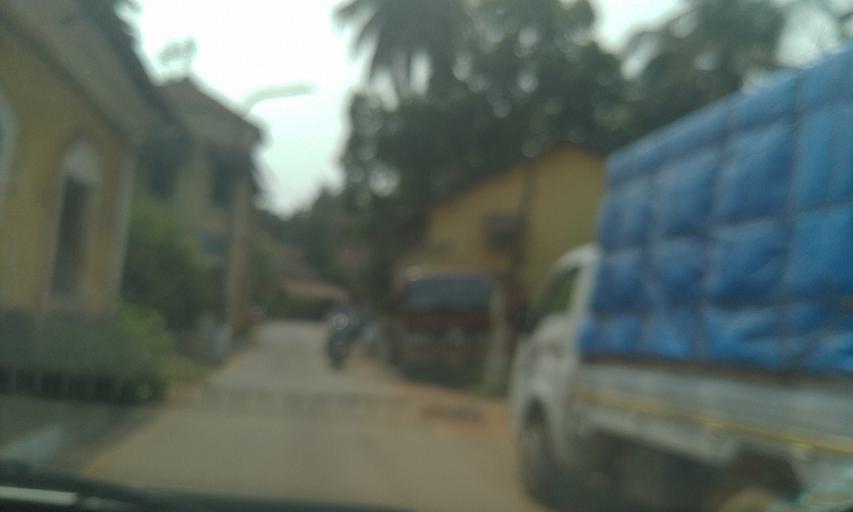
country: IN
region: Goa
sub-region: North Goa
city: Panaji
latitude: 15.4898
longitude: 73.8304
